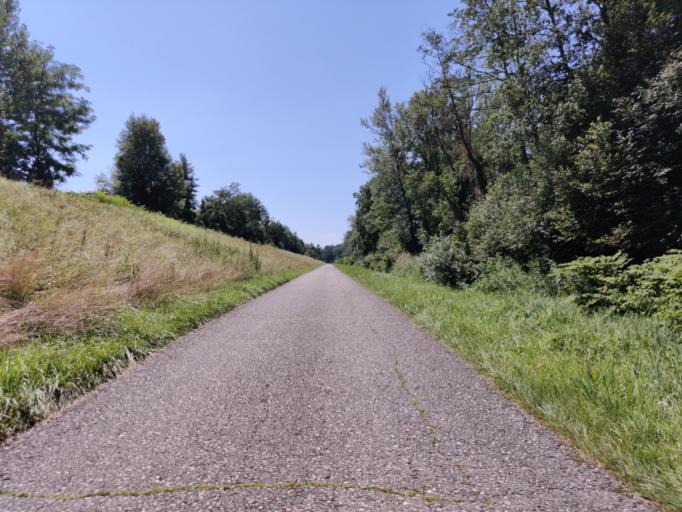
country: AT
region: Styria
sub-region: Politischer Bezirk Leibnitz
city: Gabersdorf
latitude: 46.7908
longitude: 15.5839
